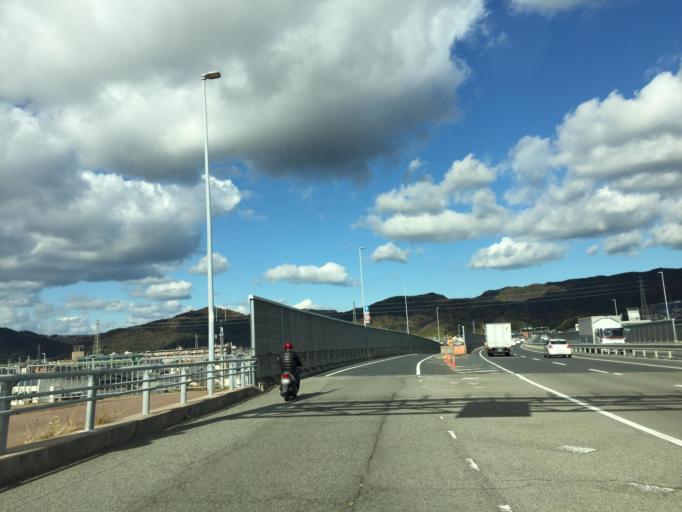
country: JP
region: Wakayama
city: Wakayama-shi
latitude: 34.2496
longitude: 135.1747
